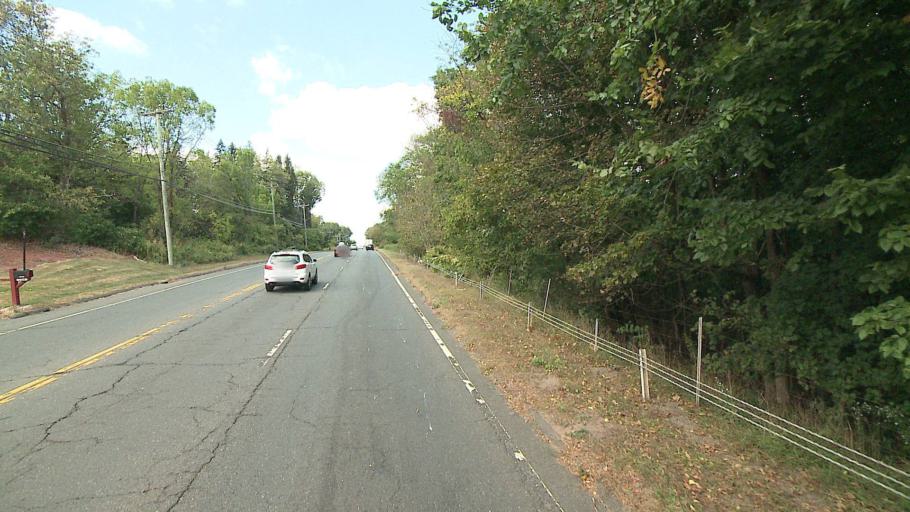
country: US
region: Connecticut
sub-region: Hartford County
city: Plainville
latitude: 41.6221
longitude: -72.8996
